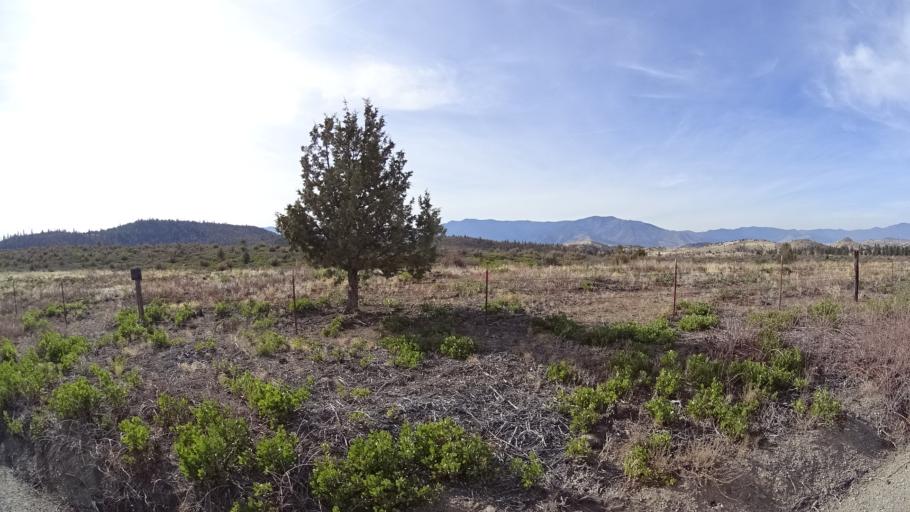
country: US
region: California
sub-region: Siskiyou County
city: Weed
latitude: 41.4840
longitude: -122.3656
